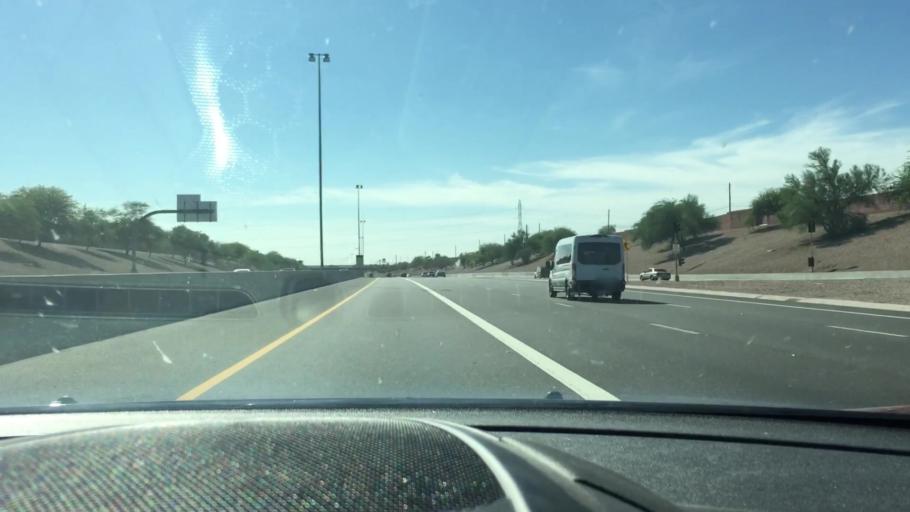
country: US
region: Arizona
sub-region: Maricopa County
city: Mesa
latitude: 33.4666
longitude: -111.7946
